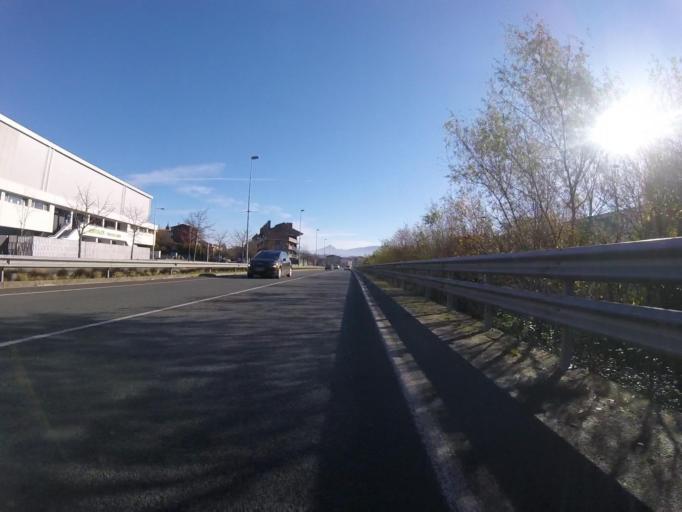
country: ES
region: Basque Country
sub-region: Provincia de Guipuzcoa
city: Fuenterrabia
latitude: 43.3623
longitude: -1.7980
